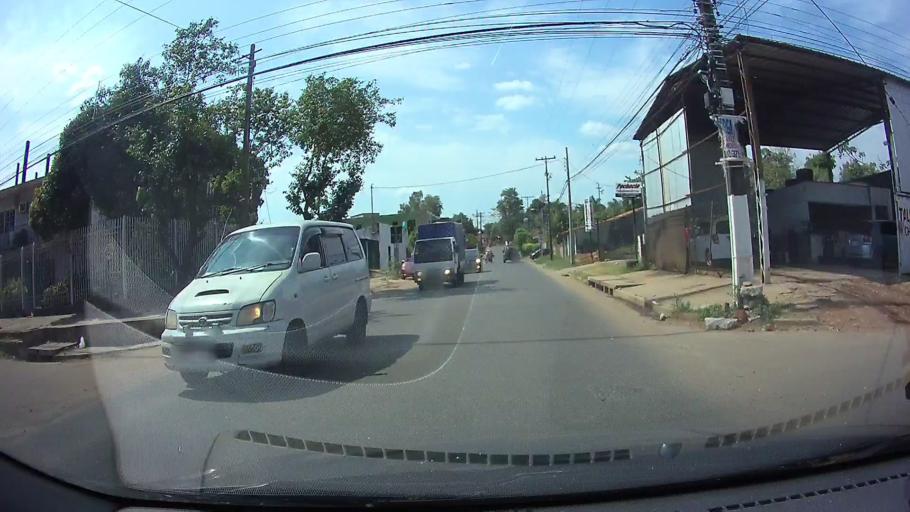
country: PY
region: Central
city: San Lorenzo
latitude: -25.3407
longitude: -57.4915
